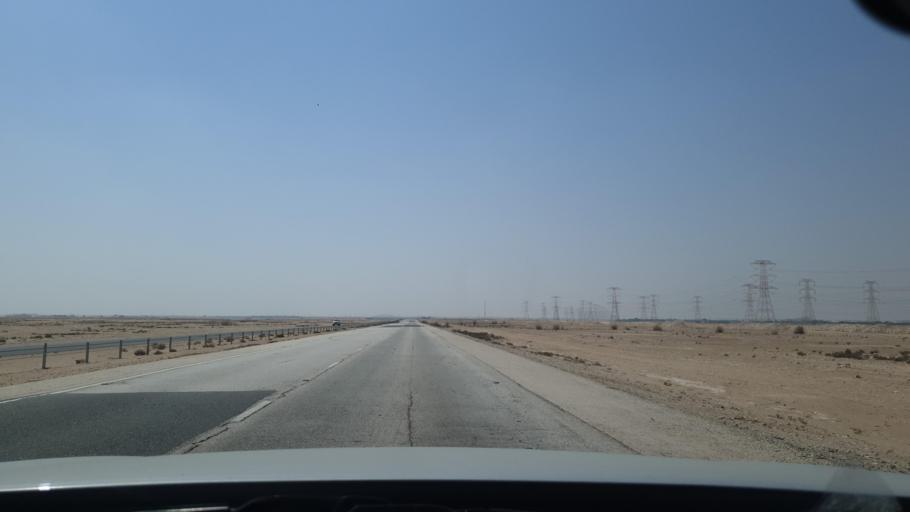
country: QA
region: Al Khawr
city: Al Khawr
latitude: 25.7092
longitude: 51.4469
